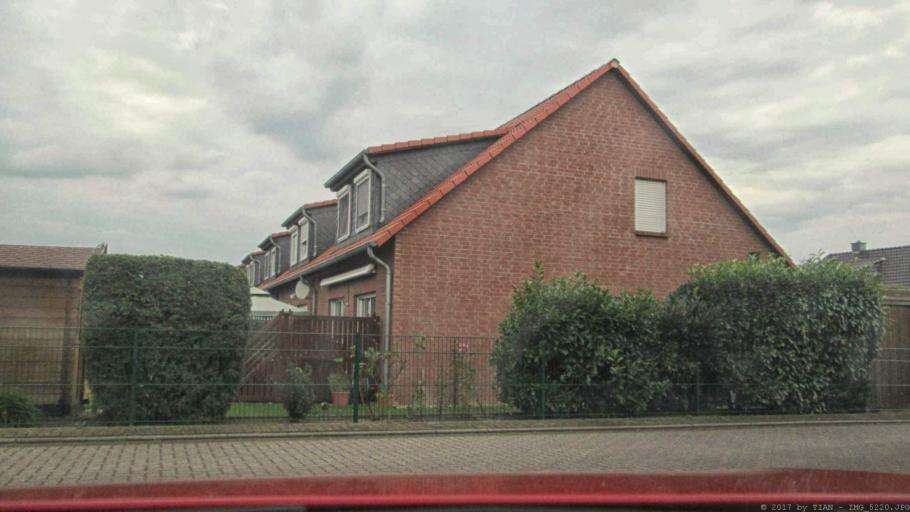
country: DE
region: Lower Saxony
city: Wolfsburg
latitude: 52.4120
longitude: 10.8451
